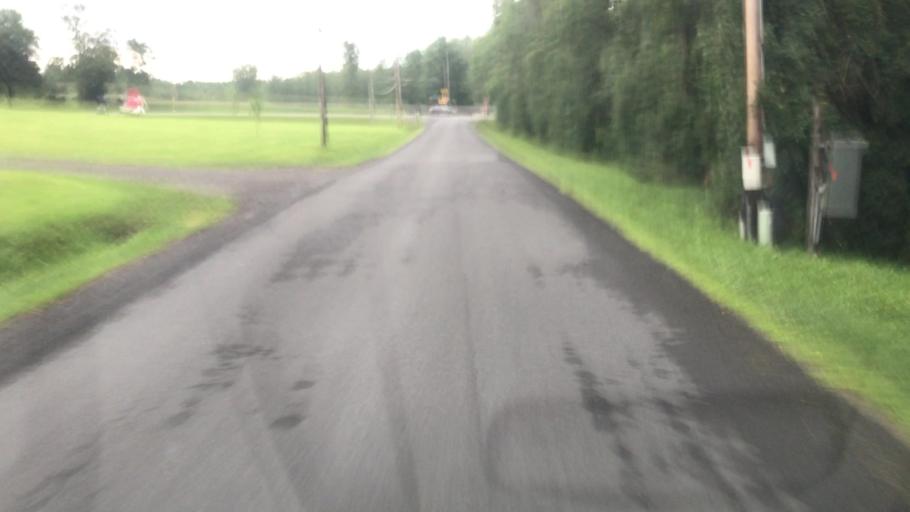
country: US
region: New York
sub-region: Cayuga County
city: Melrose Park
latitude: 42.9418
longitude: -76.4903
